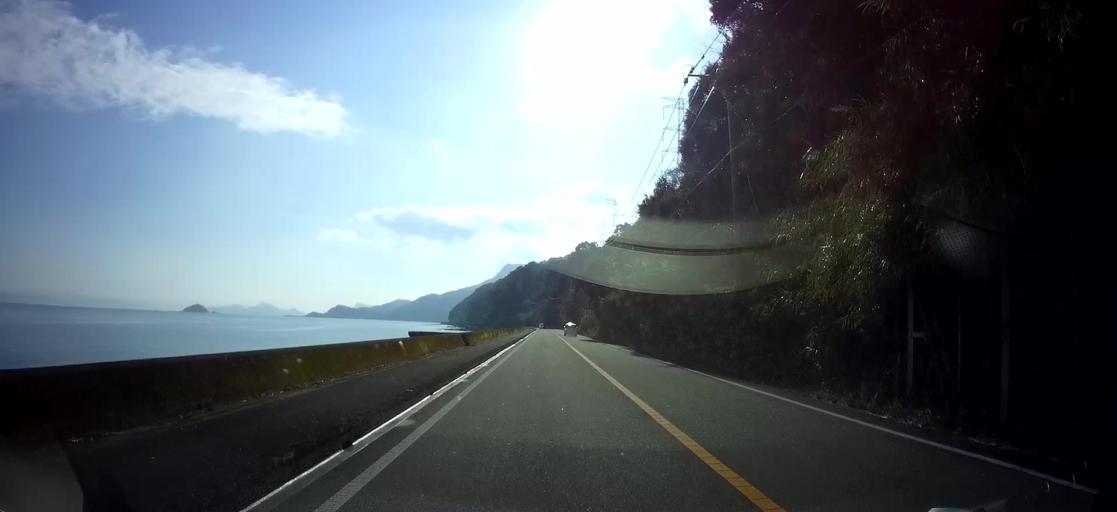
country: JP
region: Kumamoto
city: Yatsushiro
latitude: 32.5001
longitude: 130.4476
